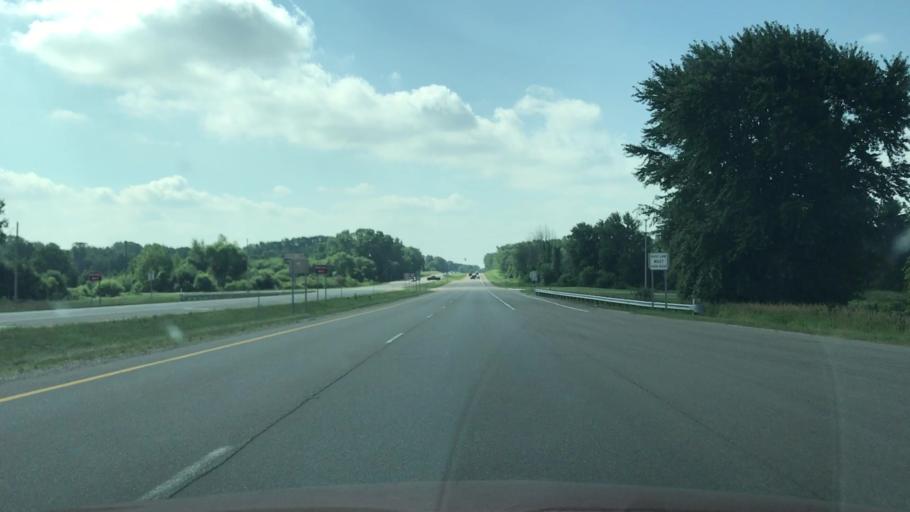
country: US
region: Michigan
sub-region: Kent County
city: Sparta
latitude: 43.1033
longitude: -85.6975
